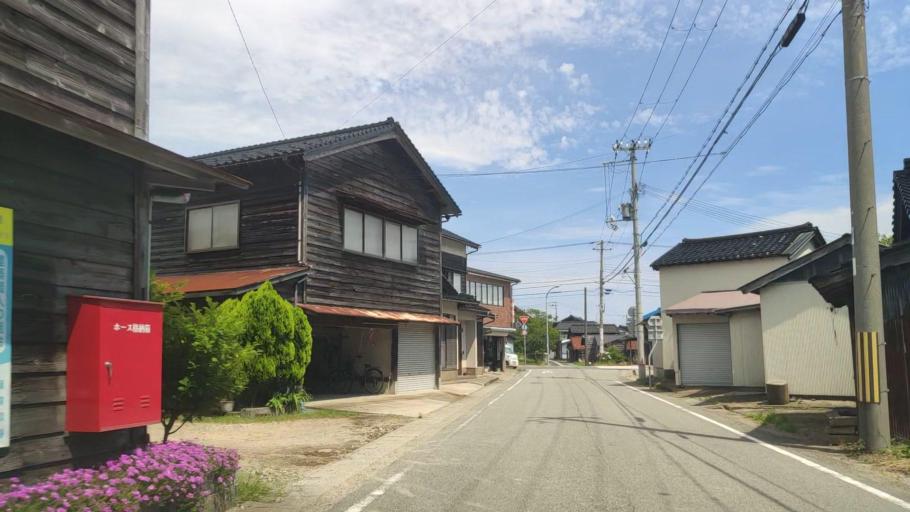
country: JP
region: Hyogo
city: Toyooka
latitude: 35.6556
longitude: 134.7624
